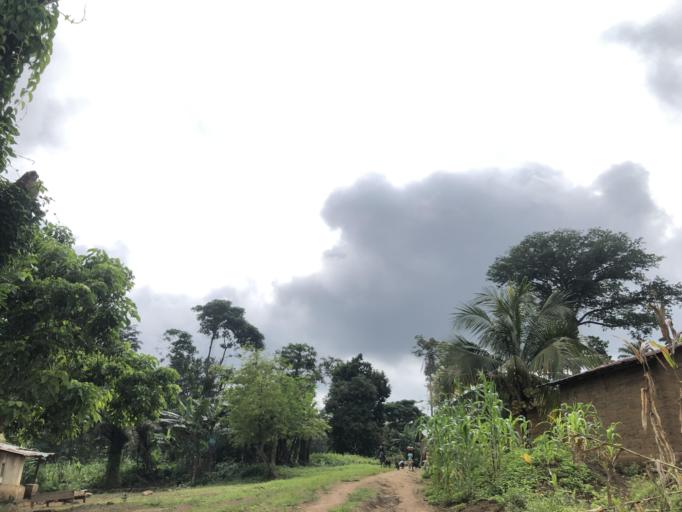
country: SL
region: Eastern Province
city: Kailahun
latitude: 8.2756
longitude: -10.5548
